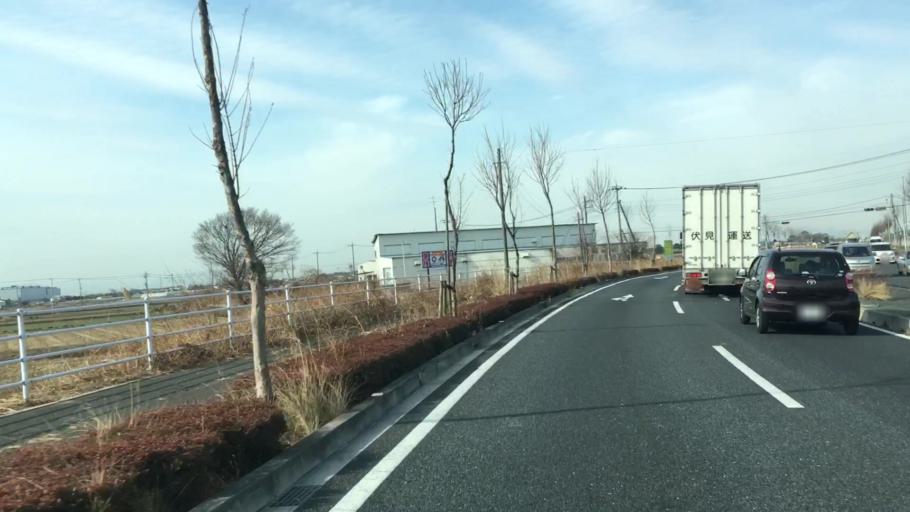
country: JP
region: Gunma
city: Tatebayashi
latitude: 36.2286
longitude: 139.4935
